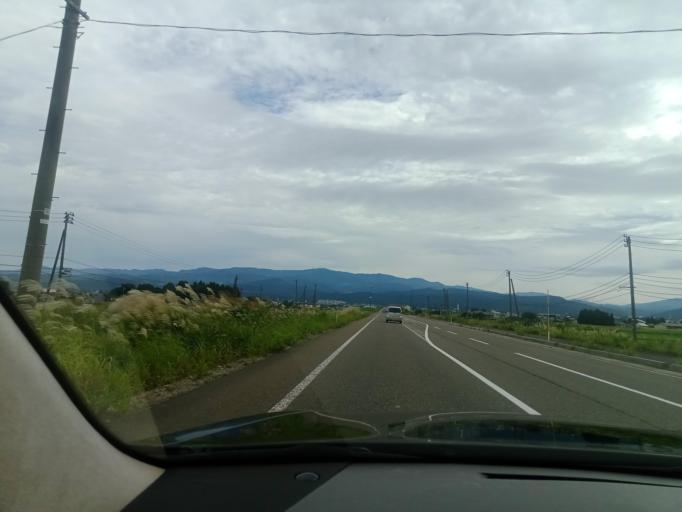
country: JP
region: Niigata
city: Arai
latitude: 37.0701
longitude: 138.2394
